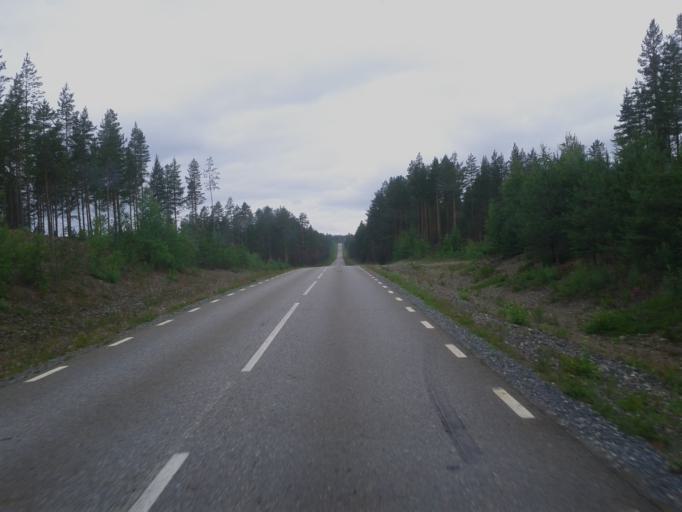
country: SE
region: Vaesterbotten
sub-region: Skelleftea Kommun
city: Kage
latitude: 64.9189
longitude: 20.9362
